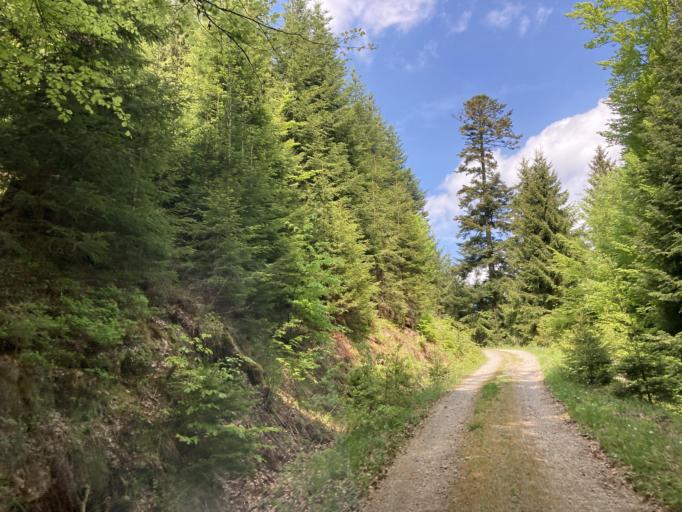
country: DE
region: Baden-Wuerttemberg
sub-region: Karlsruhe Region
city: Biberach
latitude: 48.5285
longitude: 8.2964
